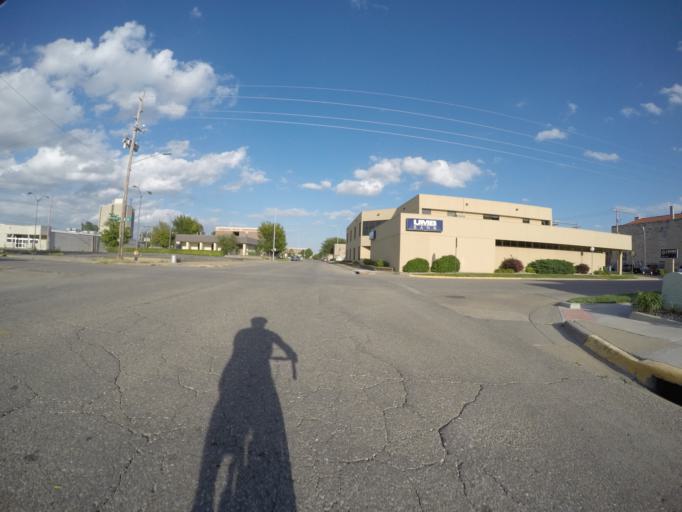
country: US
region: Kansas
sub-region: Riley County
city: Manhattan
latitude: 39.1805
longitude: -96.5652
